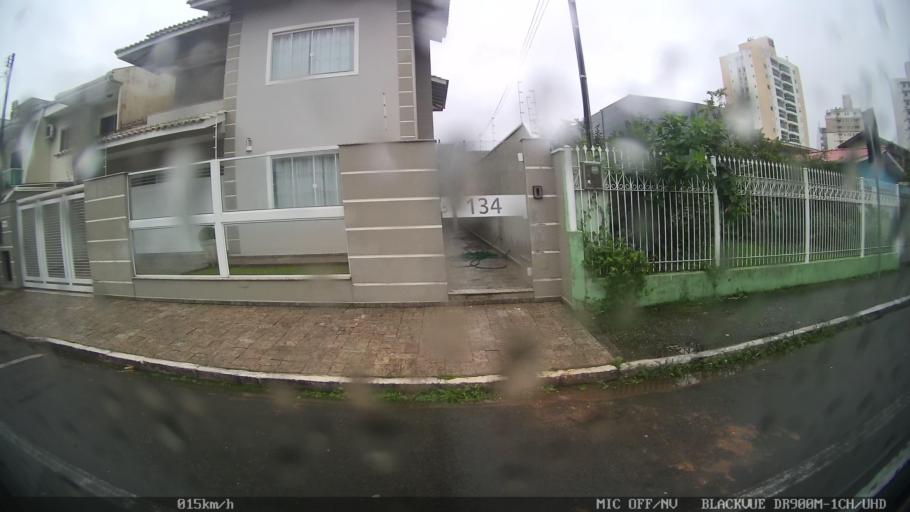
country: BR
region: Santa Catarina
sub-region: Itajai
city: Itajai
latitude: -26.9111
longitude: -48.6790
